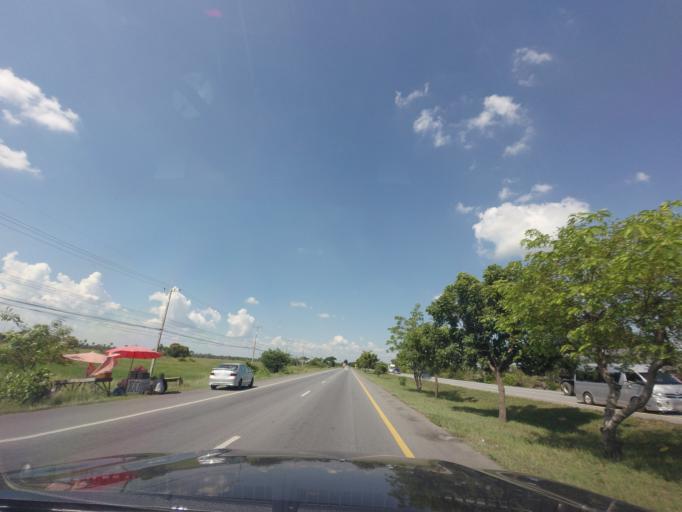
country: TH
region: Nakhon Ratchasima
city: Non Sung
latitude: 15.1322
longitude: 102.3081
